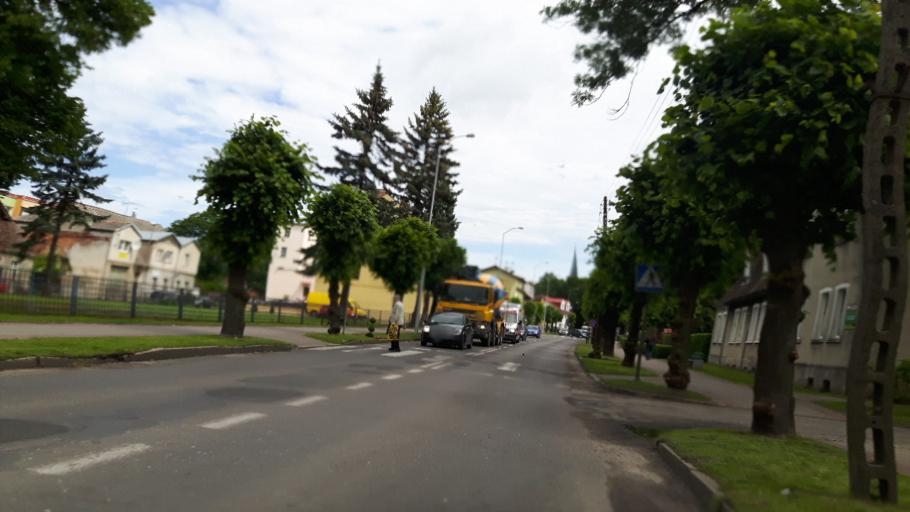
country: PL
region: West Pomeranian Voivodeship
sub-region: Powiat gryficki
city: Trzebiatow
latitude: 54.0589
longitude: 15.2618
